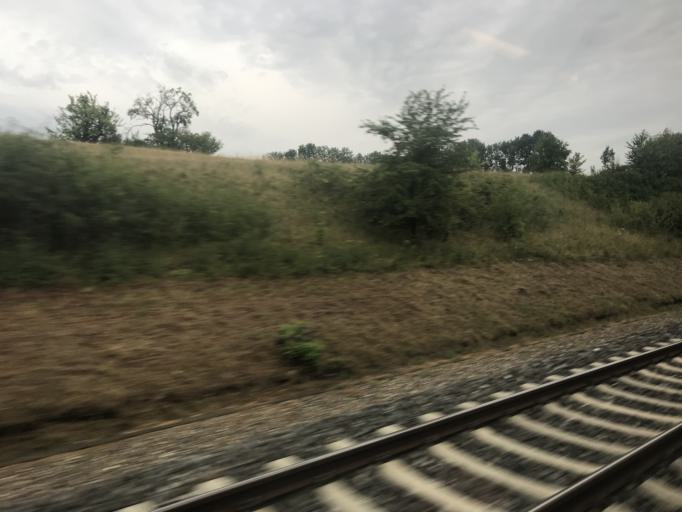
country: DE
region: Bavaria
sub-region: Regierungsbezirk Unterfranken
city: Bergtheim
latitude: 49.9173
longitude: 10.0881
